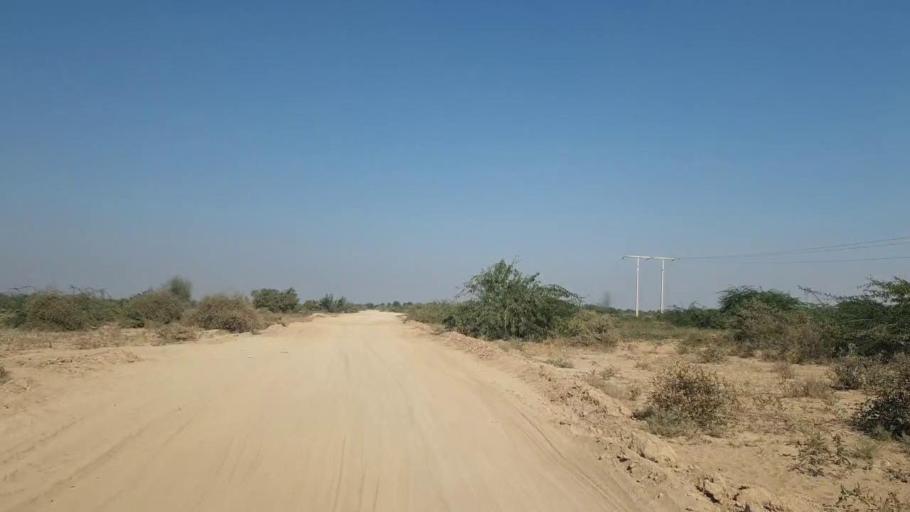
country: PK
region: Sindh
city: Jamshoro
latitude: 25.3111
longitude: 67.8184
